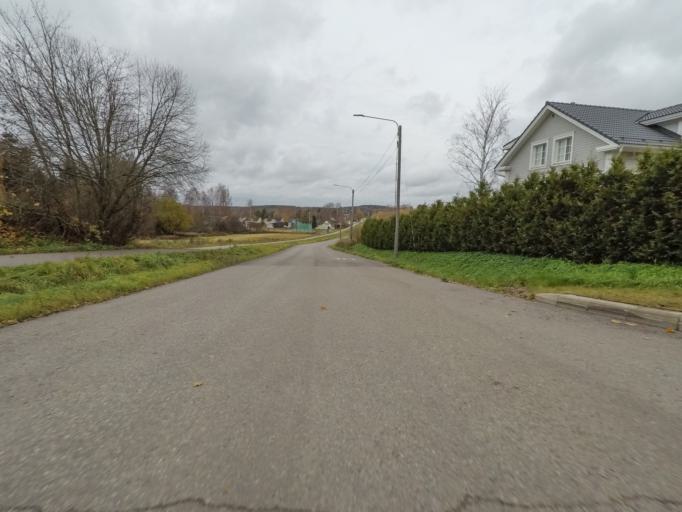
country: FI
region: Uusimaa
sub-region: Porvoo
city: Porvoo
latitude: 60.4001
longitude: 25.6550
